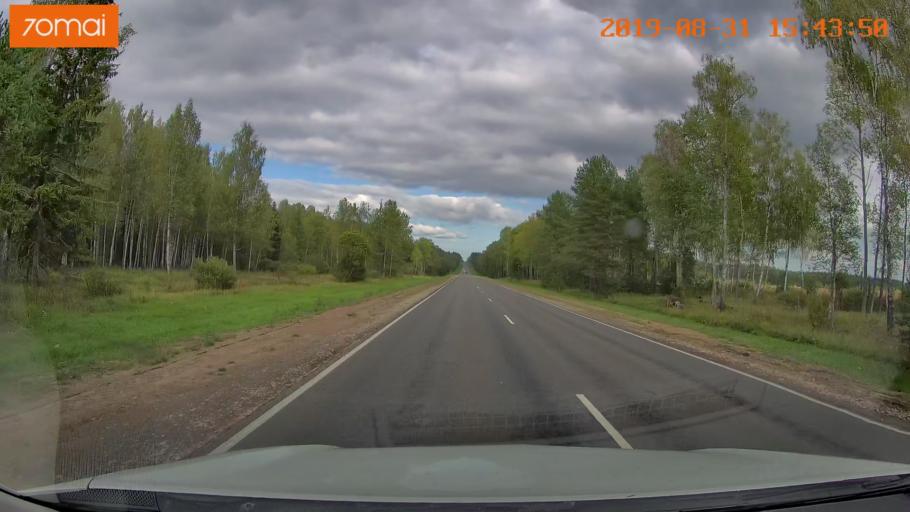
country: RU
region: Kaluga
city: Mosal'sk
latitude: 54.6550
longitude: 34.9178
